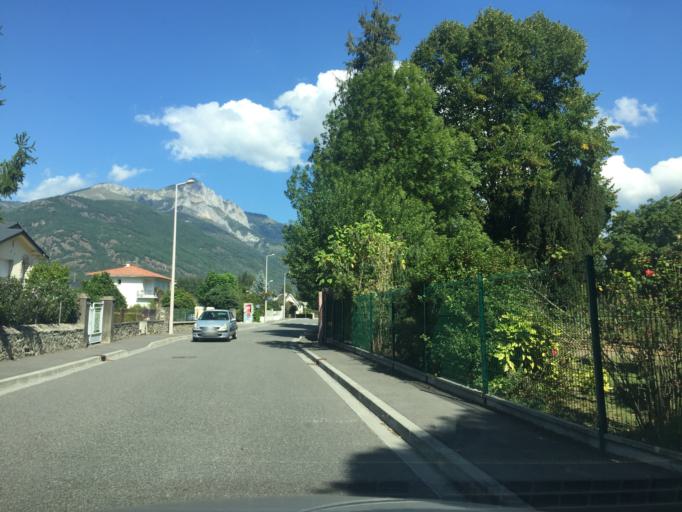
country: ES
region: Catalonia
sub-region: Provincia de Lleida
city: Les
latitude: 42.9144
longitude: 0.6427
